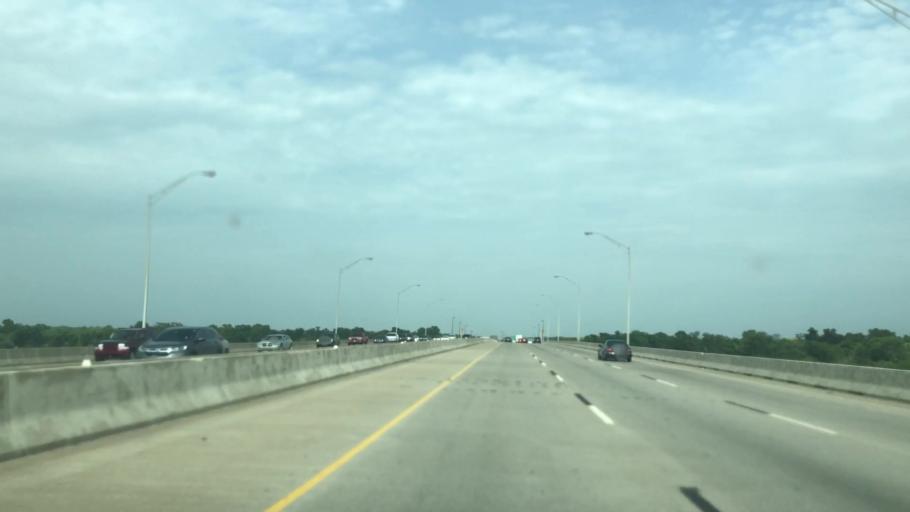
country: US
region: Oklahoma
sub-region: Tulsa County
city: Tulsa
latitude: 36.0898
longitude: -95.9911
